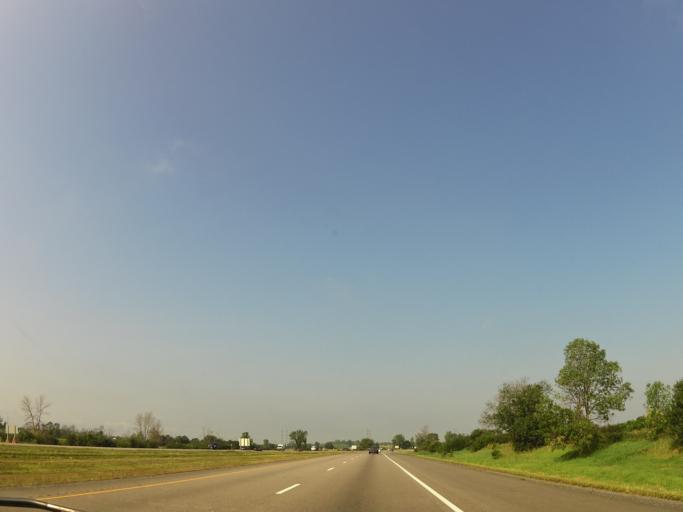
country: CA
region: Ontario
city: Napanee Downtown
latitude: 44.2554
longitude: -76.9920
